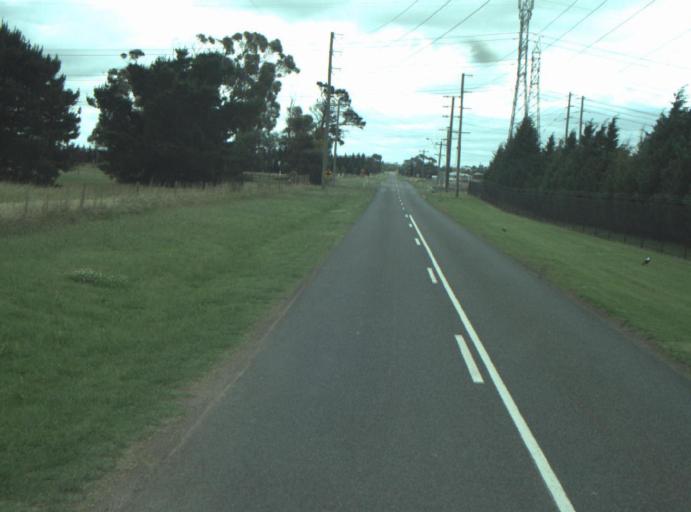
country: AU
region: Victoria
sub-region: Greater Geelong
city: Bell Post Hill
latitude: -38.0817
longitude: 144.3266
